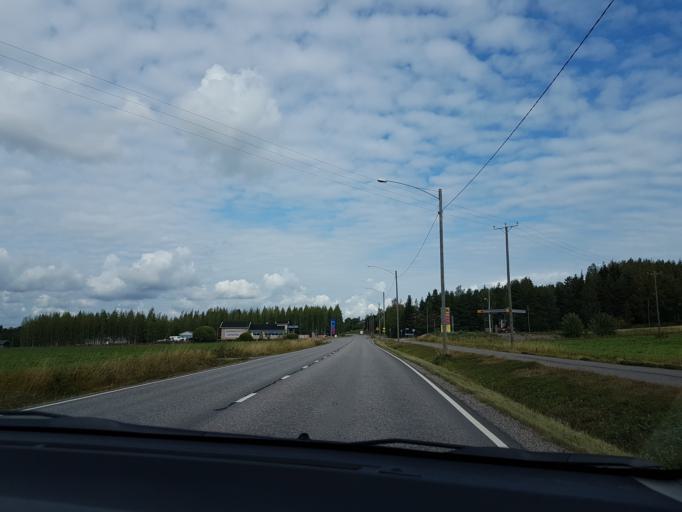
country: FI
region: Uusimaa
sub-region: Helsinki
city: Pornainen
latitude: 60.4826
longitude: 25.3700
